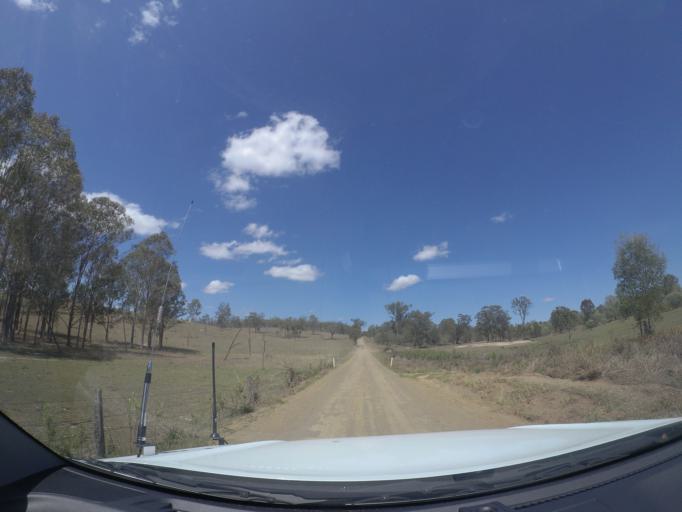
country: AU
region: Queensland
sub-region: Logan
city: Cedar Vale
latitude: -27.8523
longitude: 152.8870
